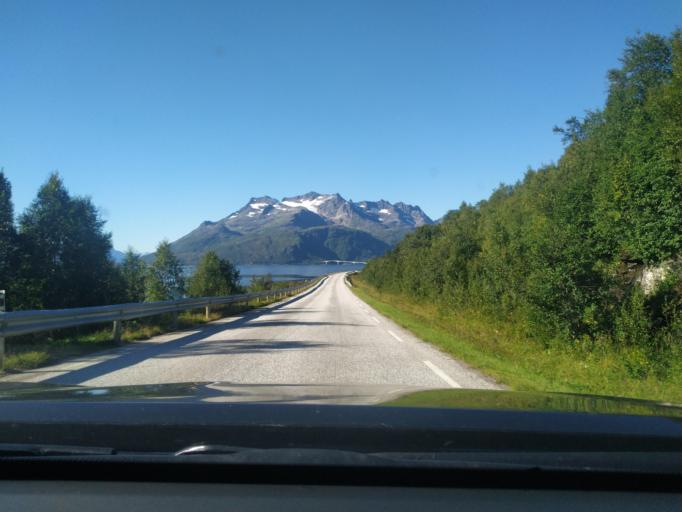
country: NO
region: Troms
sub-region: Dyroy
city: Brostadbotn
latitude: 68.9159
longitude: 17.5828
